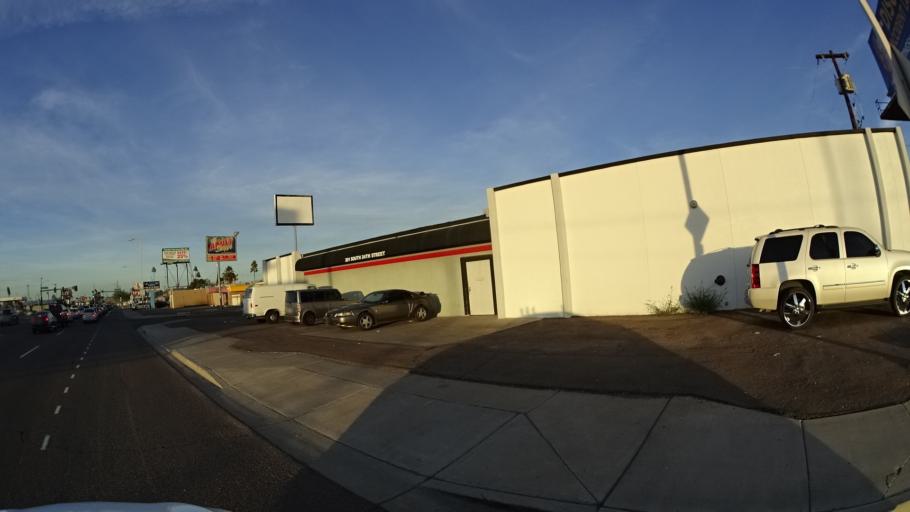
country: US
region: Arizona
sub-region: Maricopa County
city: Phoenix
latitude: 33.4459
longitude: -112.0301
